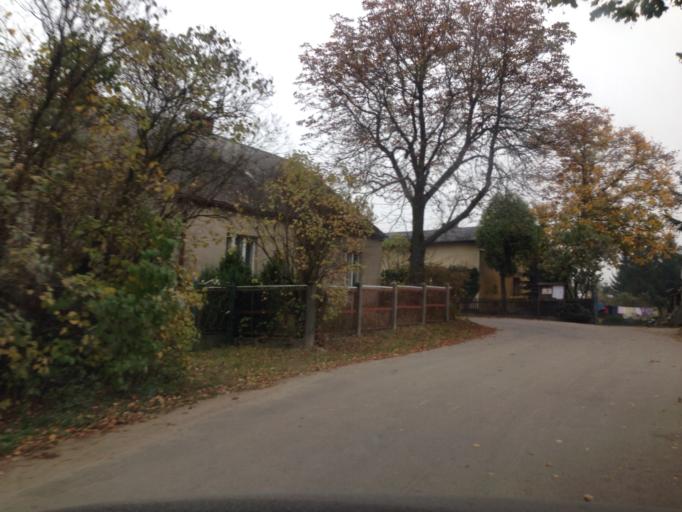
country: PL
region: Kujawsko-Pomorskie
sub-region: Powiat brodnicki
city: Bartniczka
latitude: 53.2534
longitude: 19.5150
